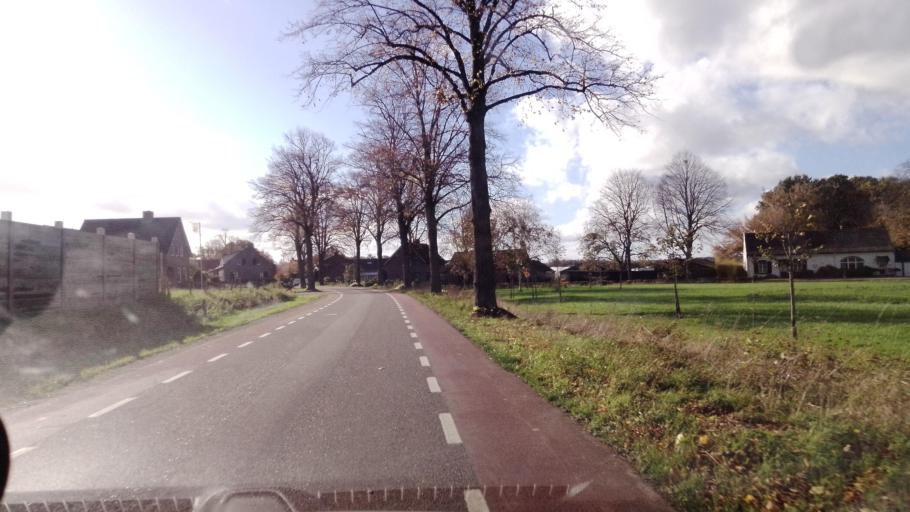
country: NL
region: Limburg
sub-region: Gemeente Venlo
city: Arcen
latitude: 51.4539
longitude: 6.1553
